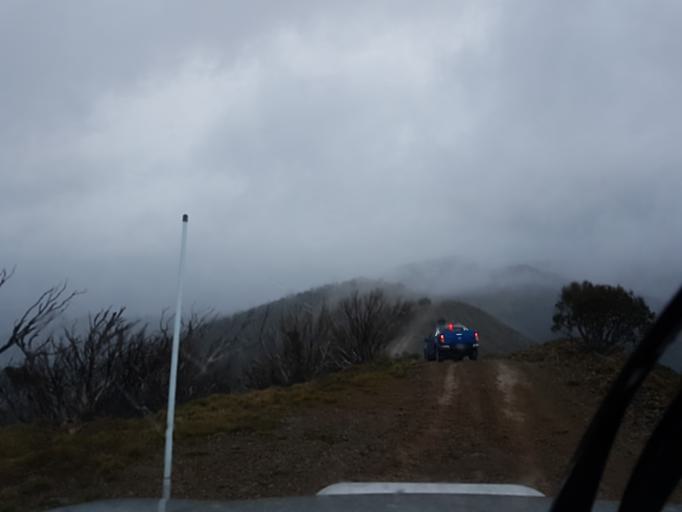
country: AU
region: Victoria
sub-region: Alpine
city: Mount Beauty
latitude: -37.0965
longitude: 147.0547
